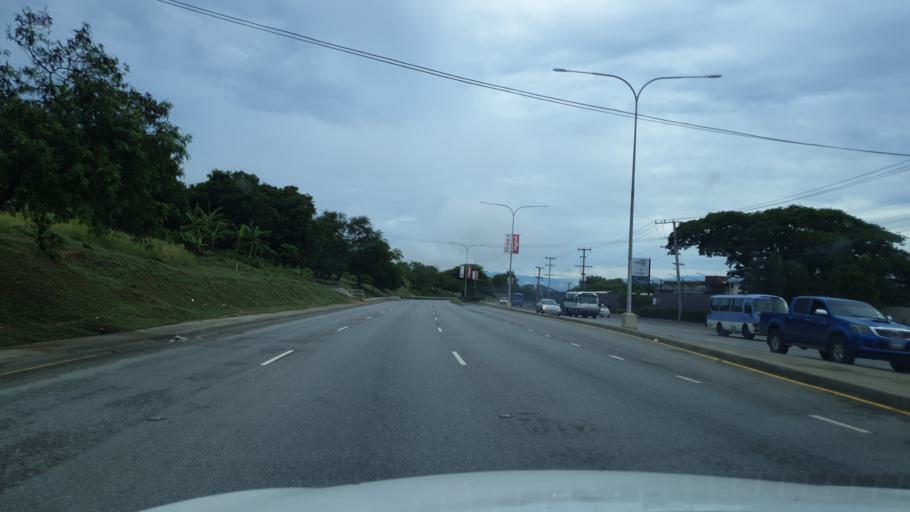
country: PG
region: National Capital
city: Port Moresby
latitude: -9.4329
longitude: 147.1793
